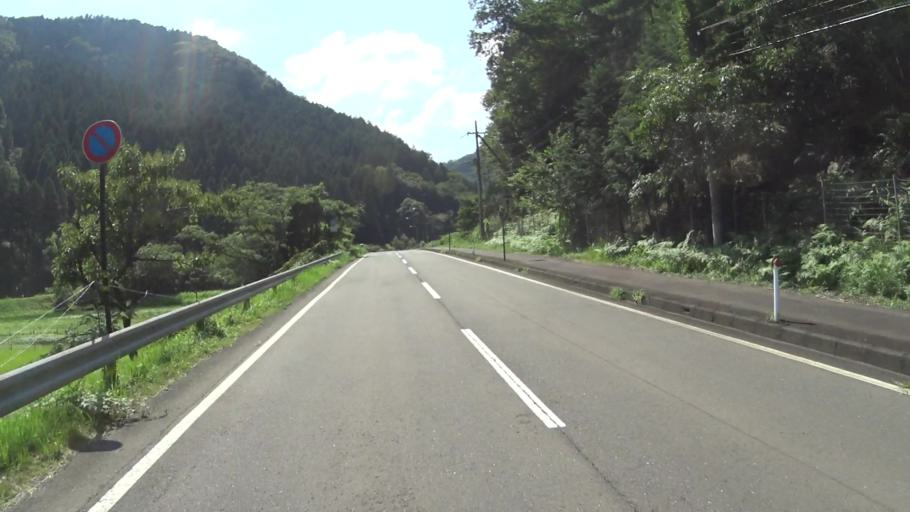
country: JP
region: Fukui
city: Obama
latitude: 35.3971
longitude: 135.6085
